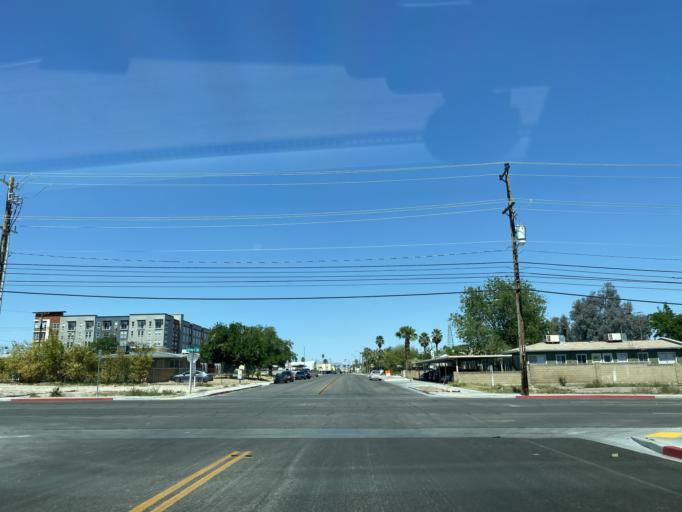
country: US
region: Nevada
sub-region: Clark County
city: Las Vegas
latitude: 36.1642
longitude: -115.1366
